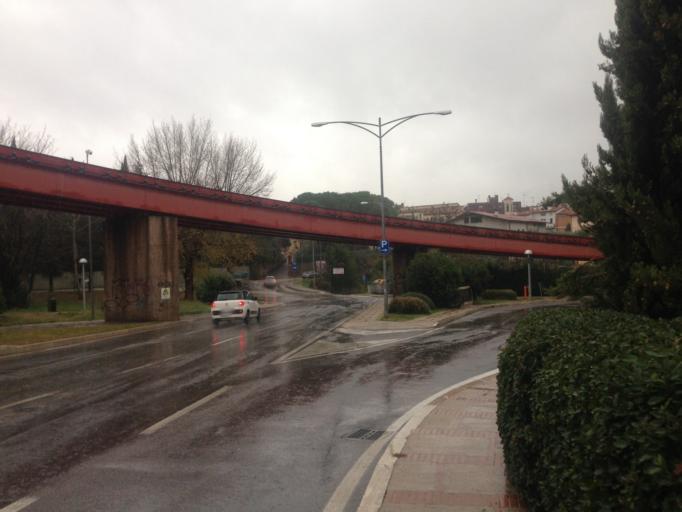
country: IT
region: Umbria
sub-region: Provincia di Perugia
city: Perugia
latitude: 43.1045
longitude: 12.3722
